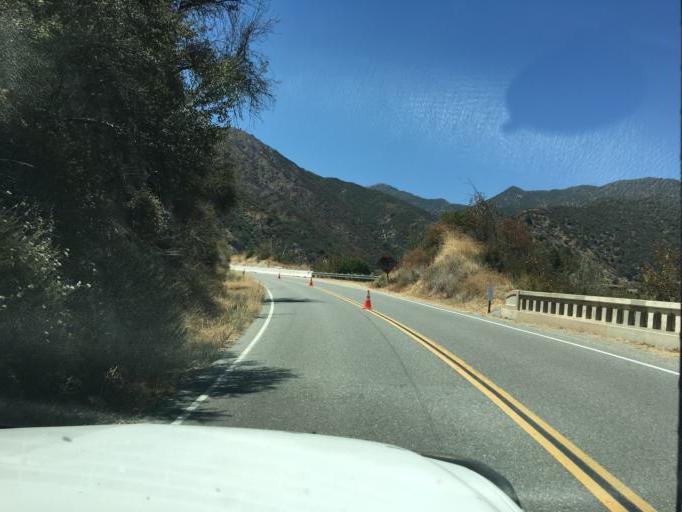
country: US
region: California
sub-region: Los Angeles County
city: Glendora
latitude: 34.2022
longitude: -117.8590
